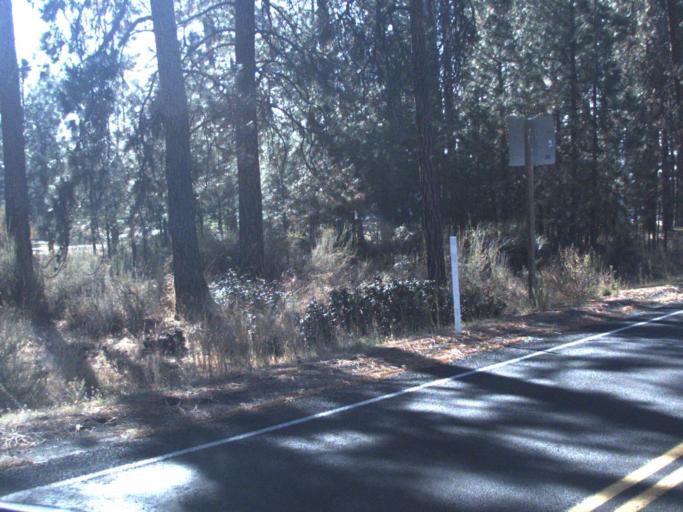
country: US
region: Washington
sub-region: Lincoln County
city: Davenport
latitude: 47.9085
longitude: -118.3125
